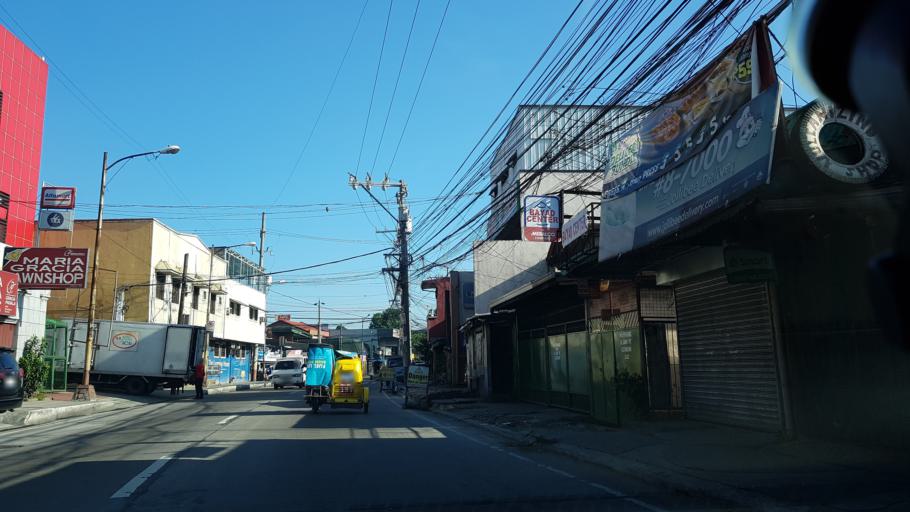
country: PH
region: Calabarzon
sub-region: Province of Rizal
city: Pateros
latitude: 14.5563
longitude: 121.0758
